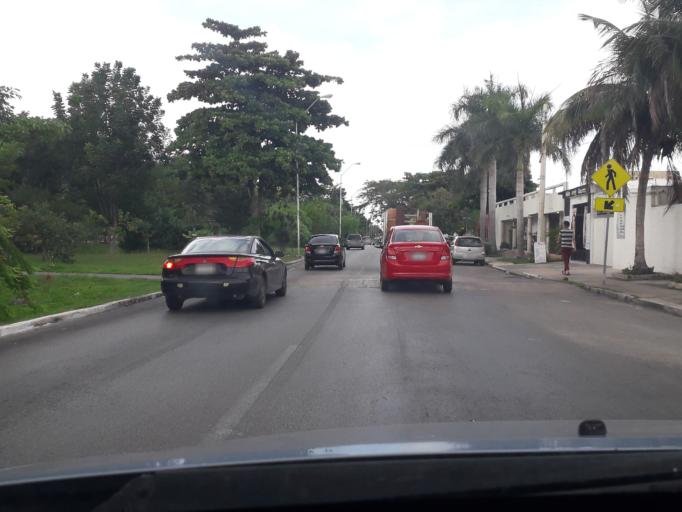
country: MX
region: Yucatan
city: Merida
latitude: 20.9819
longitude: -89.6633
